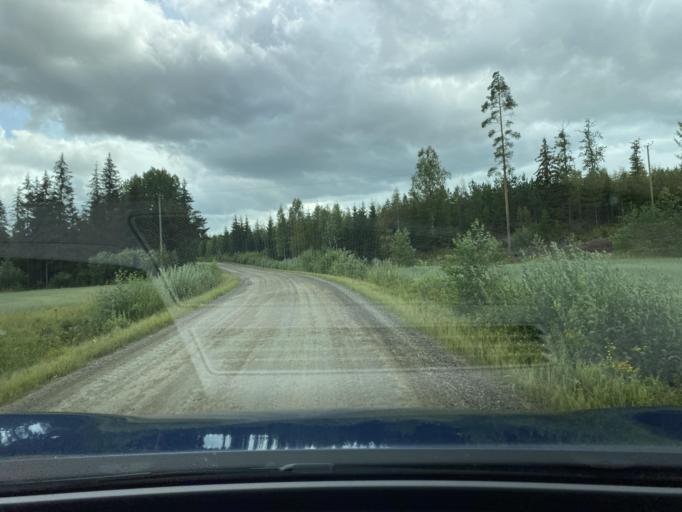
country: FI
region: Pirkanmaa
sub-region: Lounais-Pirkanmaa
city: Punkalaidun
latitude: 61.2136
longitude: 23.1688
